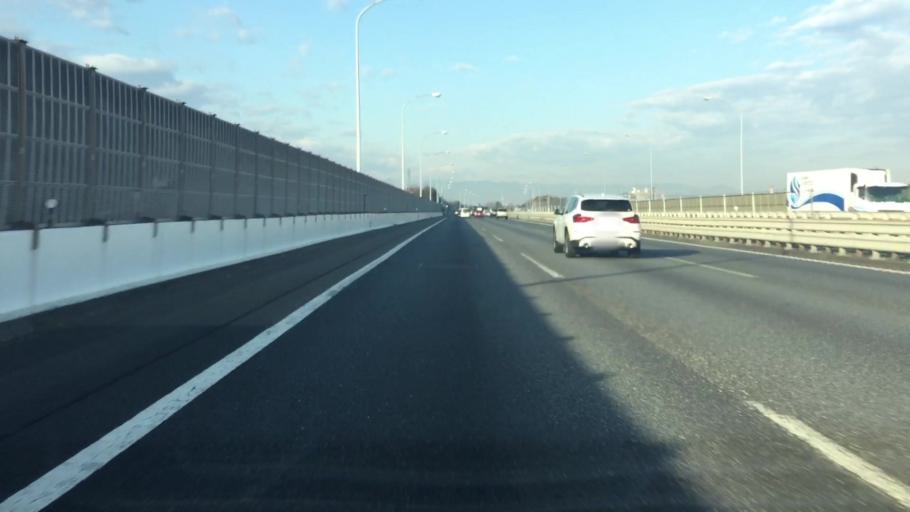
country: JP
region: Saitama
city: Kawagoe
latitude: 35.9127
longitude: 139.4352
